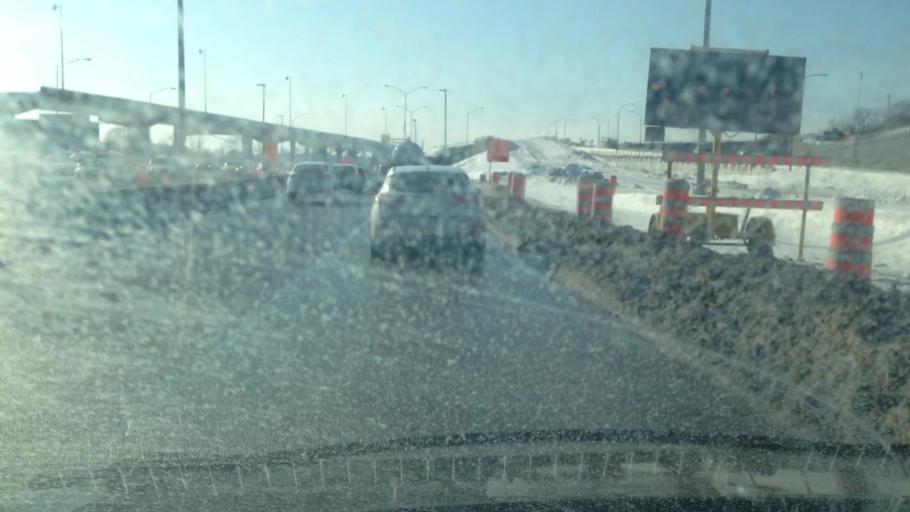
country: CA
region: Quebec
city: Montreal-Ouest
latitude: 45.4529
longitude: -73.6294
